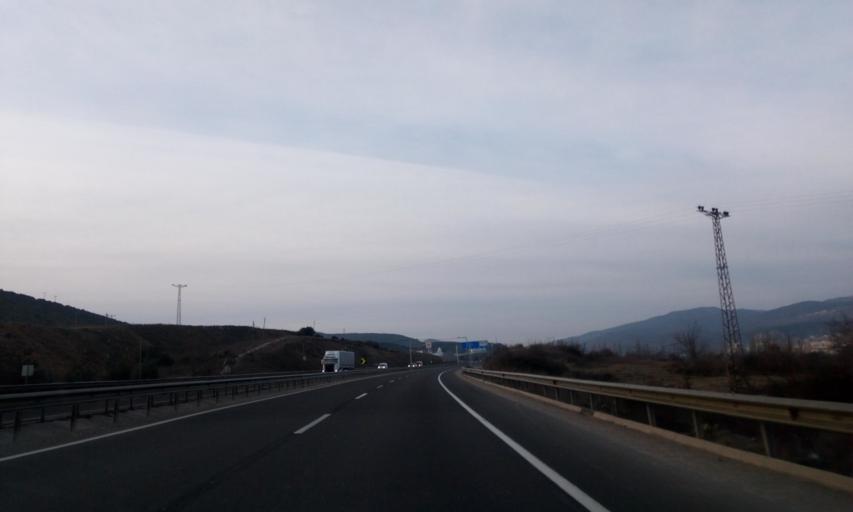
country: TR
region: Bilecik
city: Bilecik
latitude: 40.1400
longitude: 30.0255
